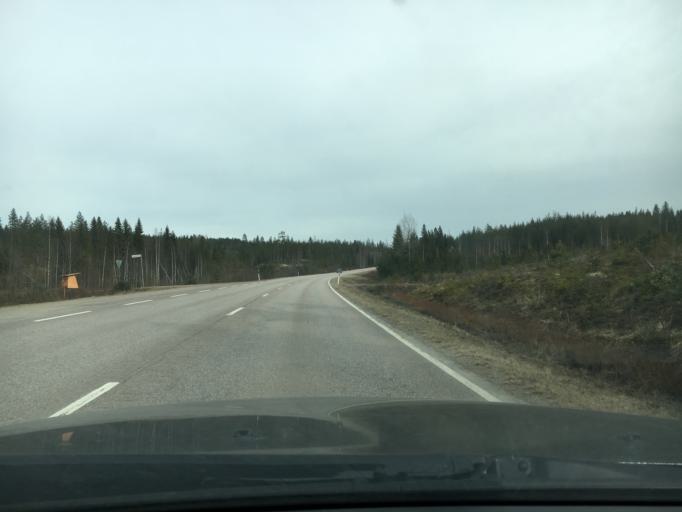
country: FI
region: Northern Savo
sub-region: Sisae-Savo
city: Rautalampi
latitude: 62.6361
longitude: 26.7285
